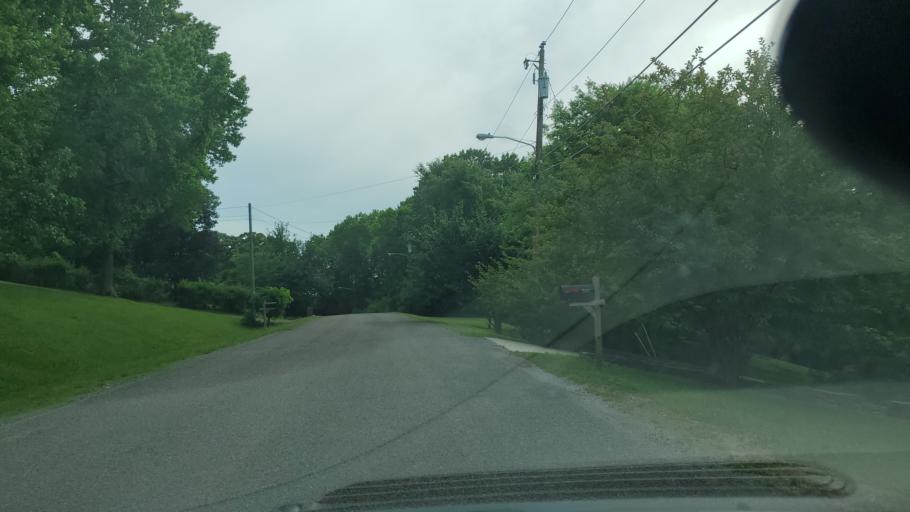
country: US
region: Tennessee
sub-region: Davidson County
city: Lakewood
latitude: 36.2182
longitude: -86.6862
